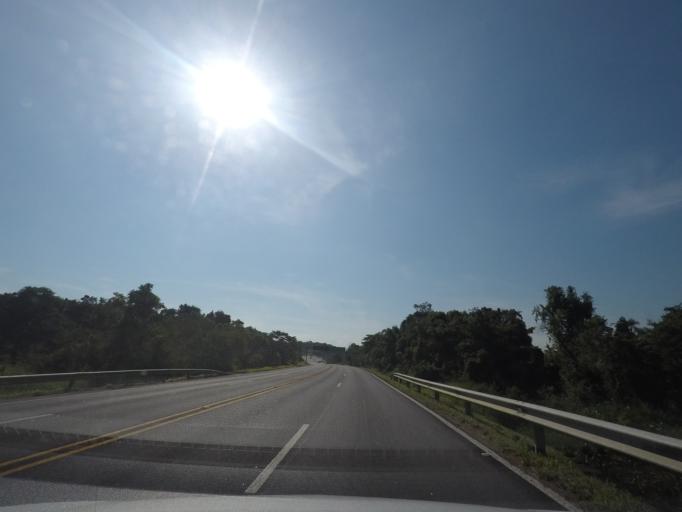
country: BR
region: Parana
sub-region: Paranagua
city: Paranagua
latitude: -25.5738
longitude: -48.6130
